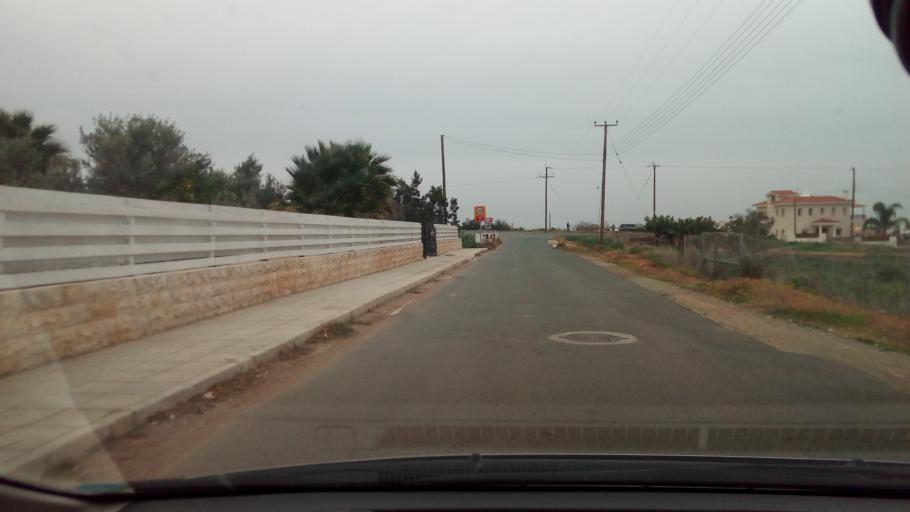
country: CY
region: Pafos
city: Empa
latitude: 34.8040
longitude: 32.4193
